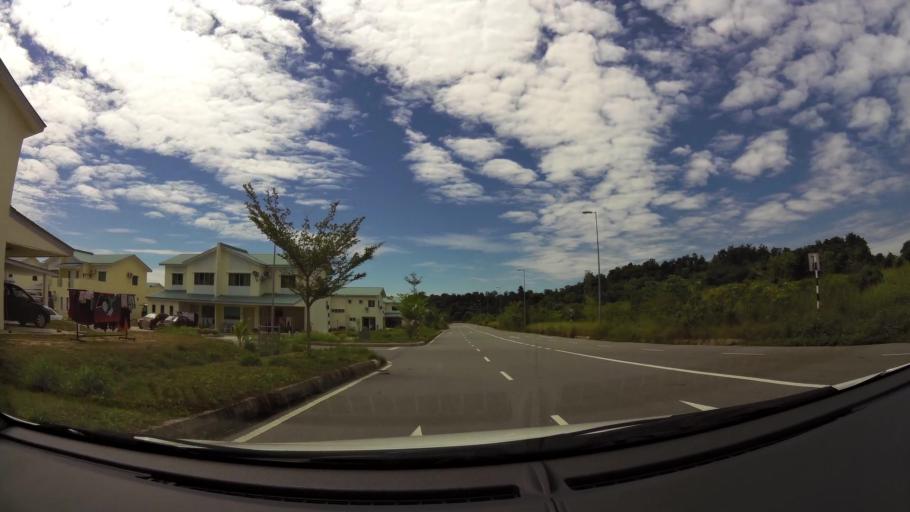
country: BN
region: Brunei and Muara
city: Bandar Seri Begawan
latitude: 4.9725
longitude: 115.0118
